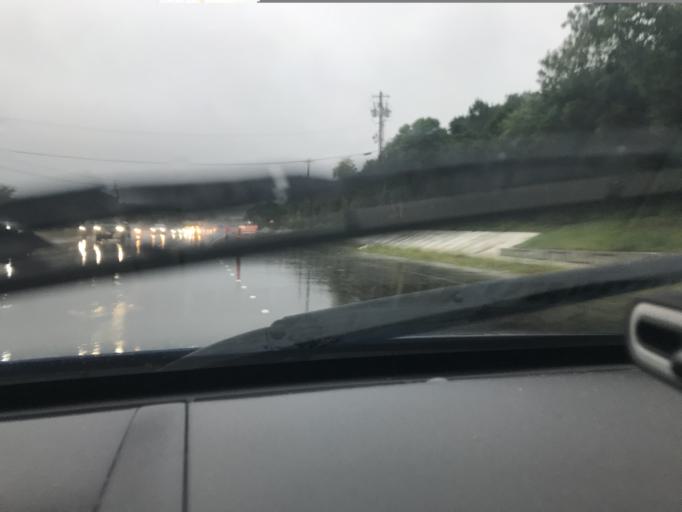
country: US
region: Texas
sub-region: Travis County
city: West Lake Hills
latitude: 30.2897
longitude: -97.8189
